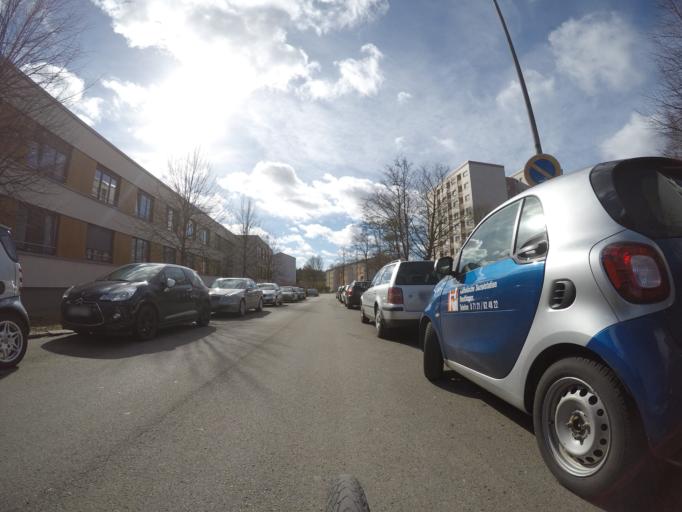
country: DE
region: Baden-Wuerttemberg
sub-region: Tuebingen Region
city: Sickenhausen
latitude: 48.5182
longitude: 9.2028
